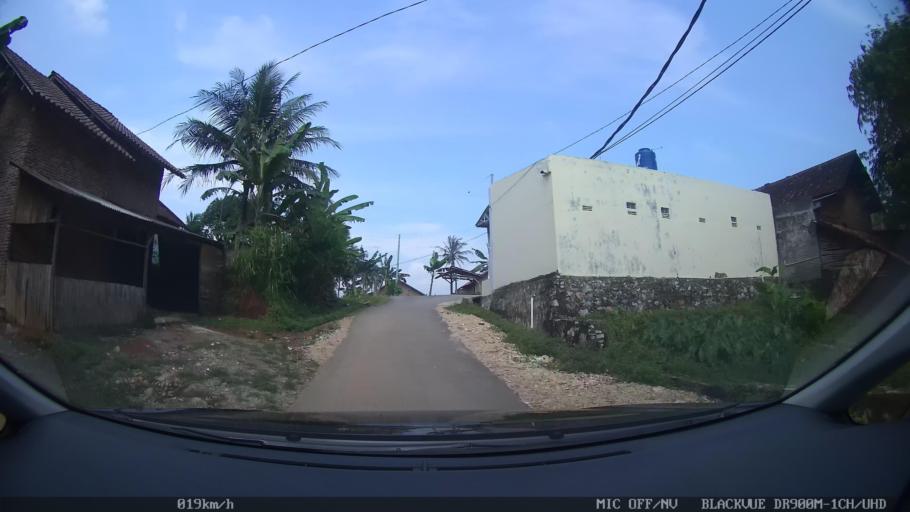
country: ID
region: Lampung
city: Kedaton
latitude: -5.3290
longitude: 105.2731
